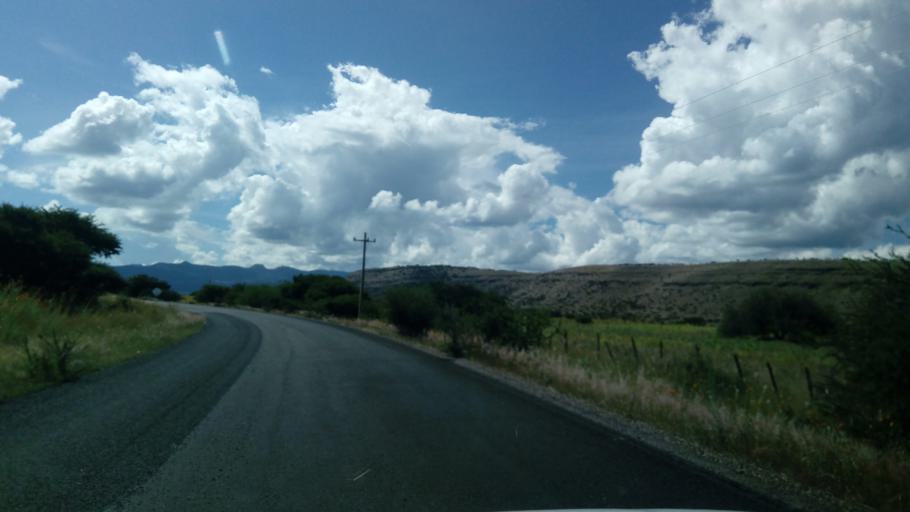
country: MX
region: Durango
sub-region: Durango
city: Jose Refugio Salcido
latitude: 23.8292
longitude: -104.4823
